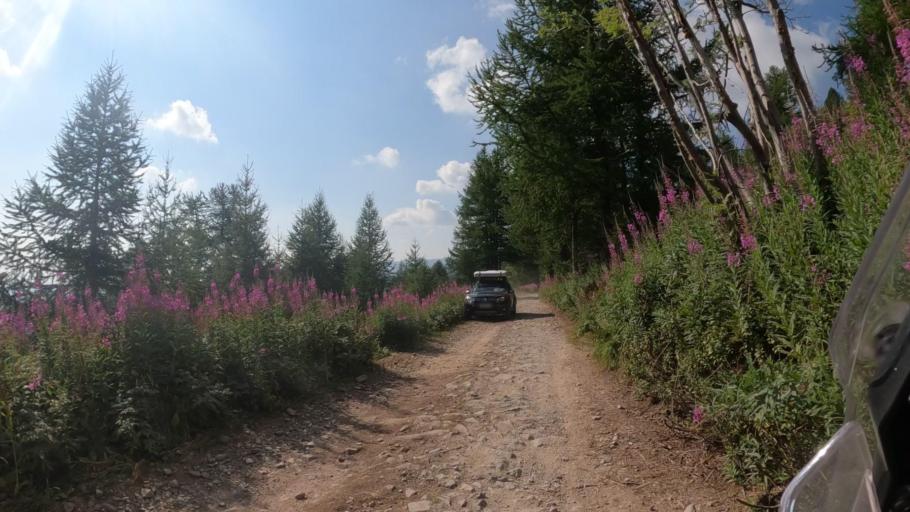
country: IT
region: Piedmont
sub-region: Provincia di Cuneo
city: Briga Alta
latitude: 44.1267
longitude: 7.6915
